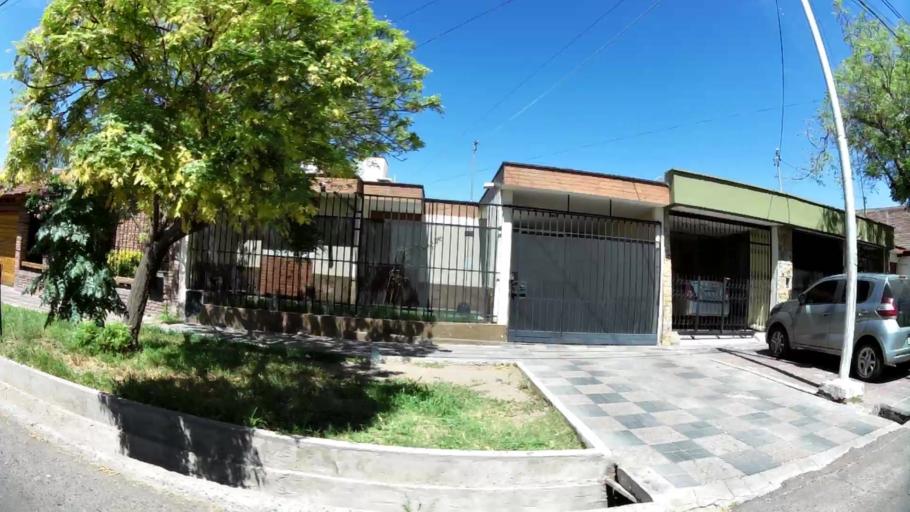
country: AR
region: Mendoza
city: Las Heras
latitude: -32.8411
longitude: -68.8650
